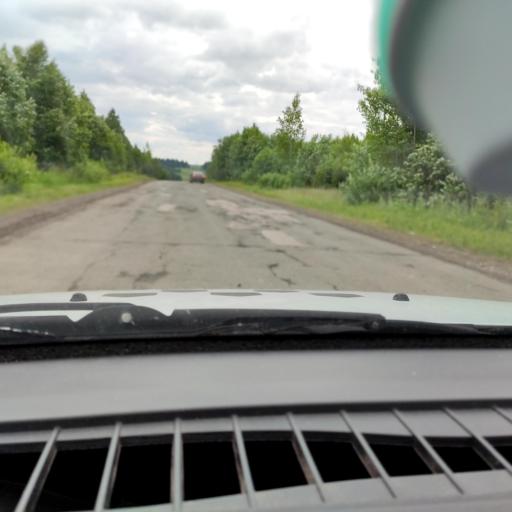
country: RU
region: Perm
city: Uinskoye
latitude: 57.1244
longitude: 56.5550
